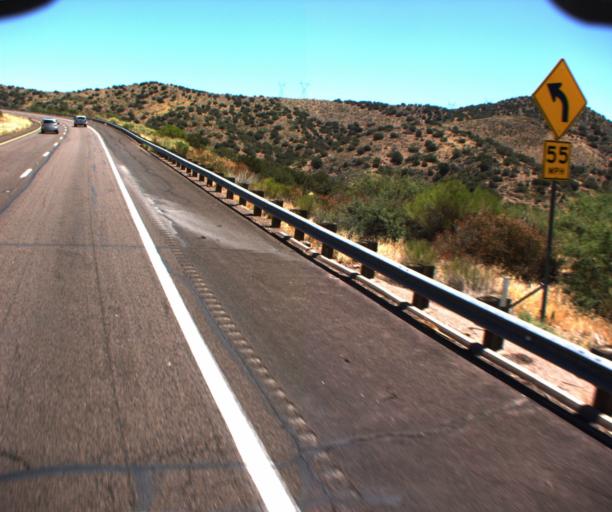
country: US
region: Arizona
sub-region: Gila County
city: Tonto Basin
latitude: 33.9824
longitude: -111.3844
